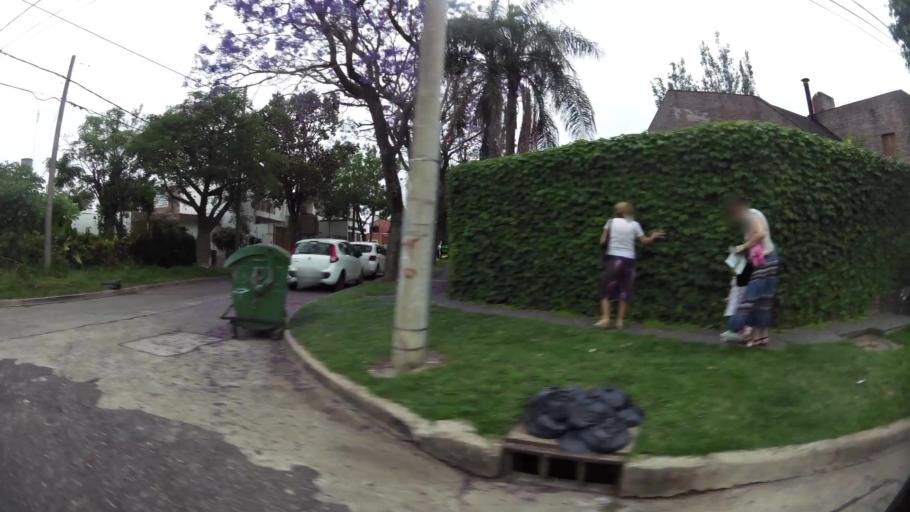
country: AR
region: Santa Fe
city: Granadero Baigorria
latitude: -32.8743
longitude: -60.6919
